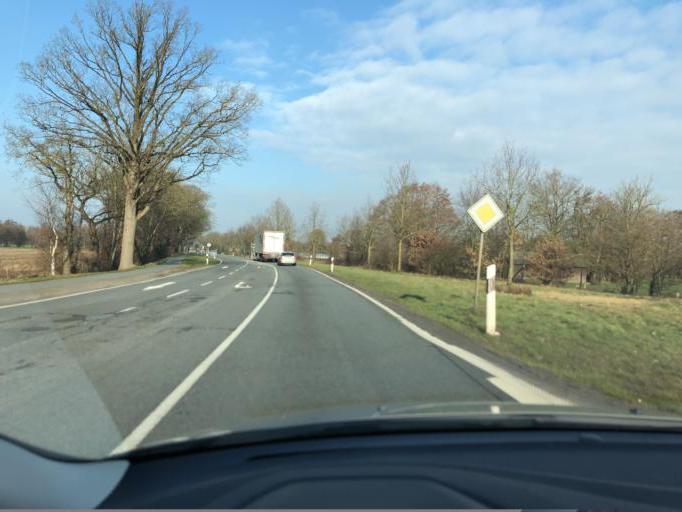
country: DE
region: Lower Saxony
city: Westerstede
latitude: 53.2810
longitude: 7.9011
